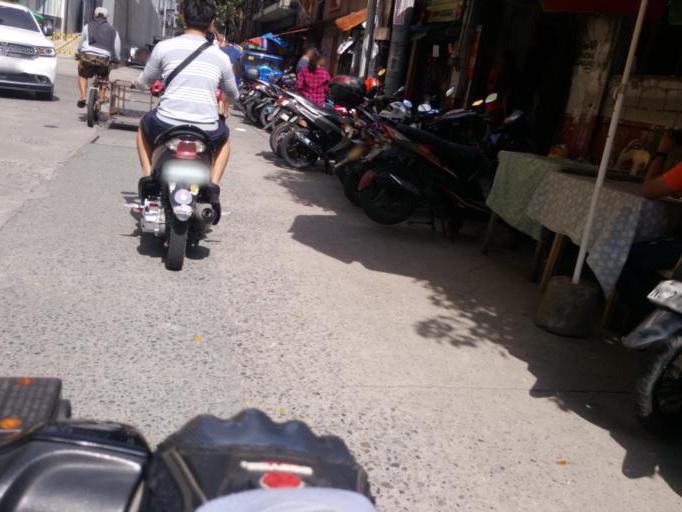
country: PH
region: Metro Manila
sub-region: City of Manila
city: Manila
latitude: 14.6170
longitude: 120.9864
